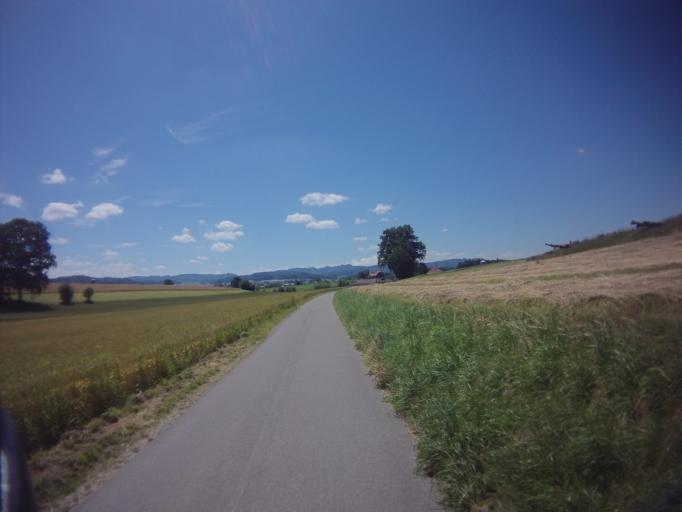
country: CH
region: Bern
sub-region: Bern-Mittelland District
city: Fraubrunnen
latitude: 47.0658
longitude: 7.5377
